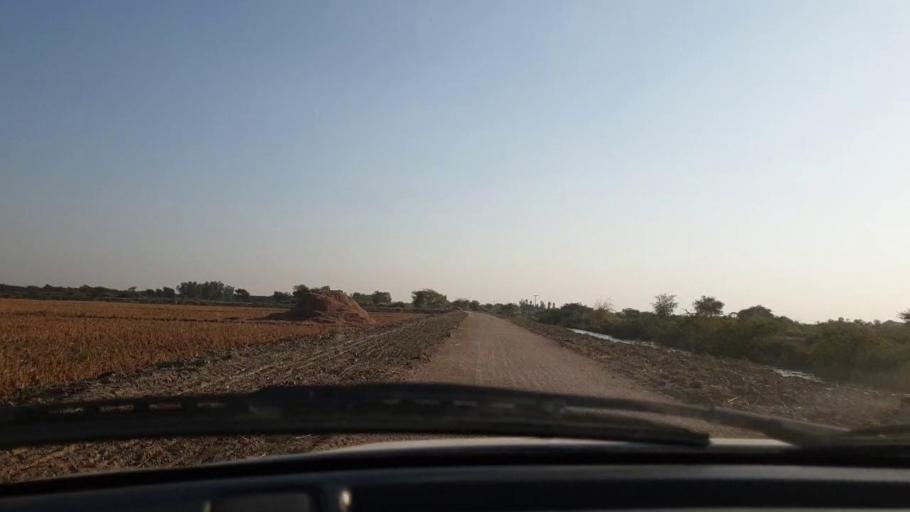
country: PK
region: Sindh
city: Bulri
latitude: 24.8042
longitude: 68.3963
